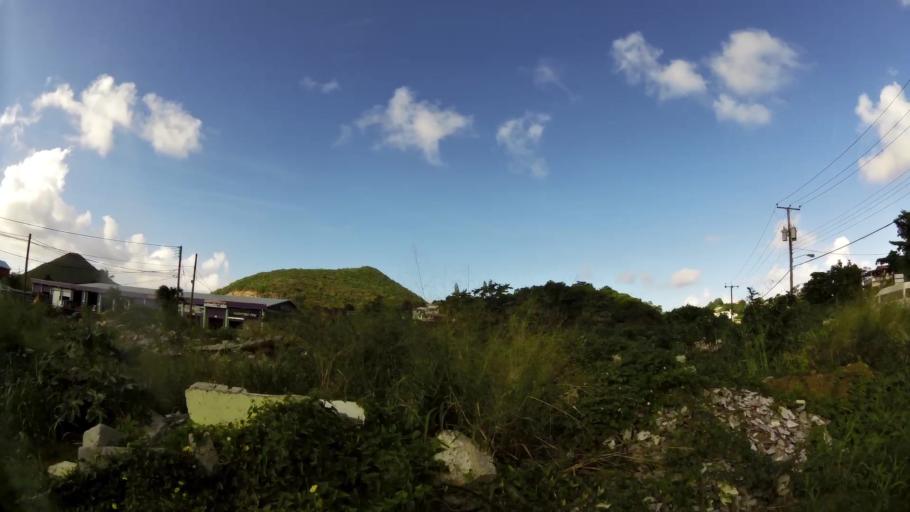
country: LC
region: Gros-Islet
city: Gros Islet
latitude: 14.0581
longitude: -60.9588
